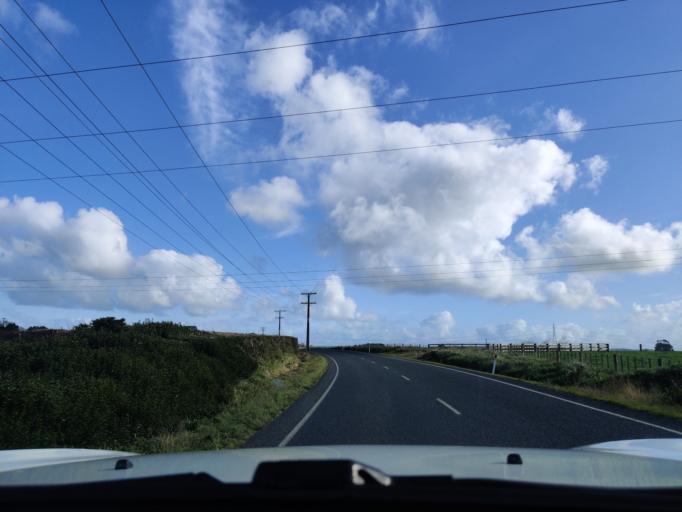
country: NZ
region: Waikato
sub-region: Waikato District
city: Te Kauwhata
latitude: -37.3603
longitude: 175.2548
